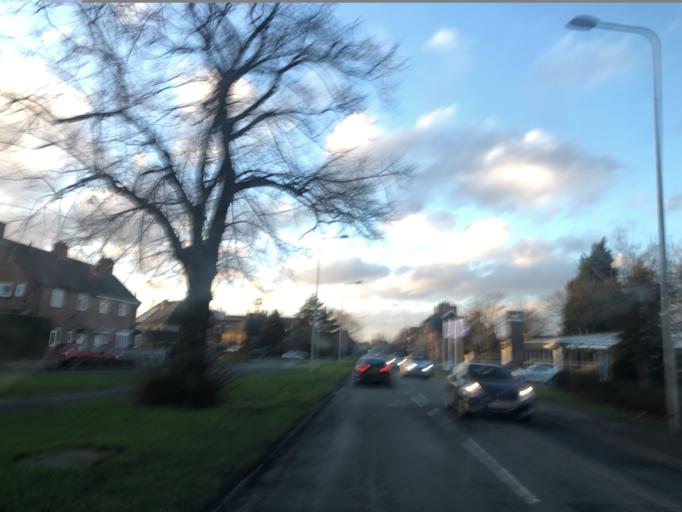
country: GB
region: England
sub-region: Cheshire West and Chester
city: Marston
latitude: 53.2589
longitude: -2.4927
